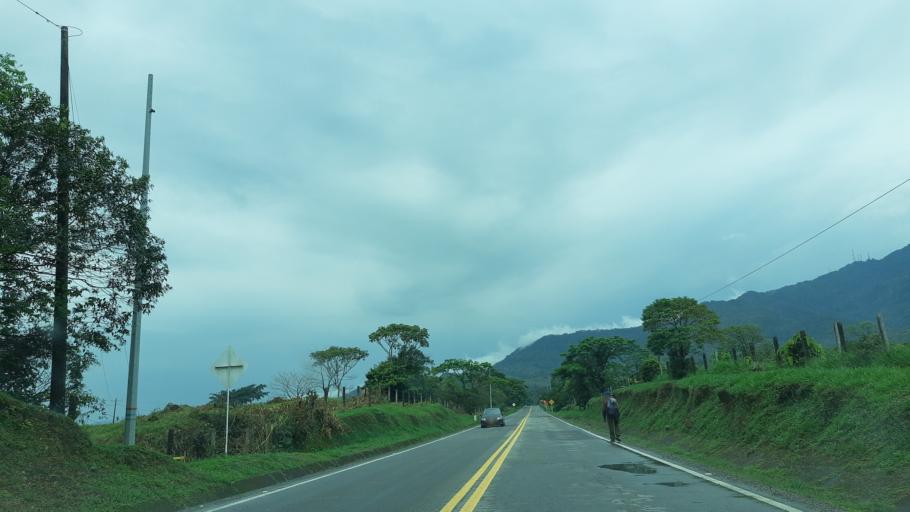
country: CO
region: Casanare
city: Monterrey
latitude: 4.8433
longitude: -72.9475
